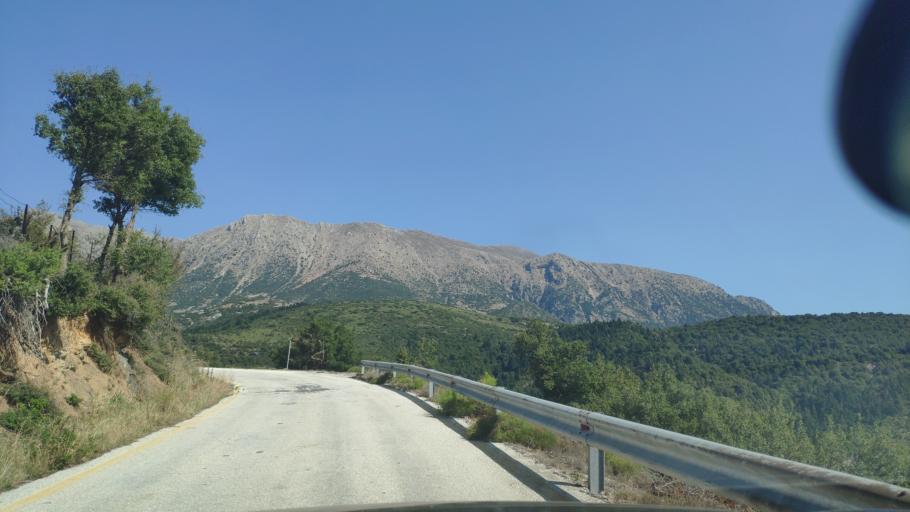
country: GR
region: Peloponnese
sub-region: Nomos Korinthias
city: Nemea
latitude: 37.8652
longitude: 22.3873
